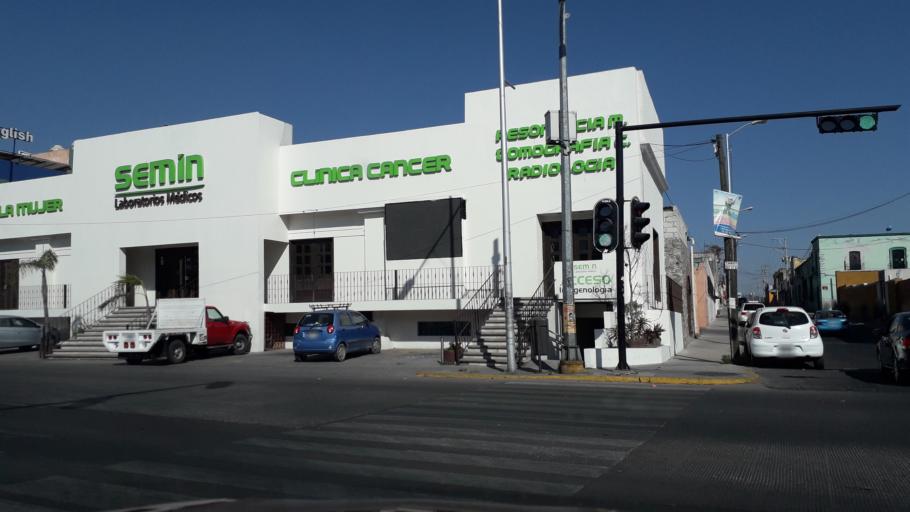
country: MX
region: Puebla
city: Puebla
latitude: 19.0391
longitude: -98.1959
